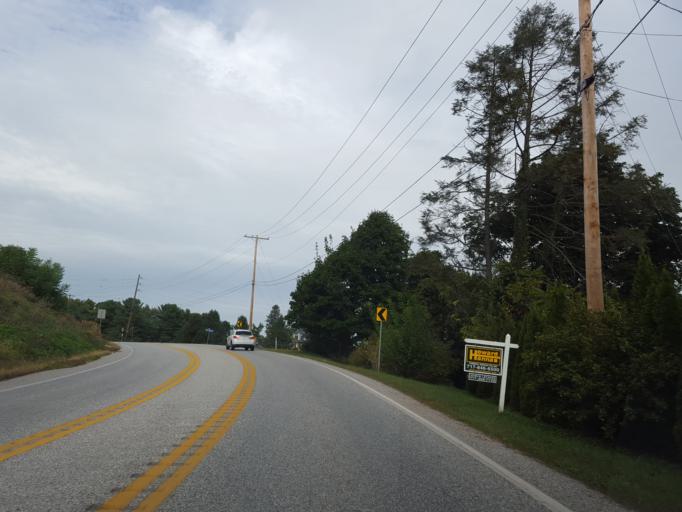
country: US
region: Pennsylvania
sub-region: York County
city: Yoe
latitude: 39.9310
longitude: -76.6560
